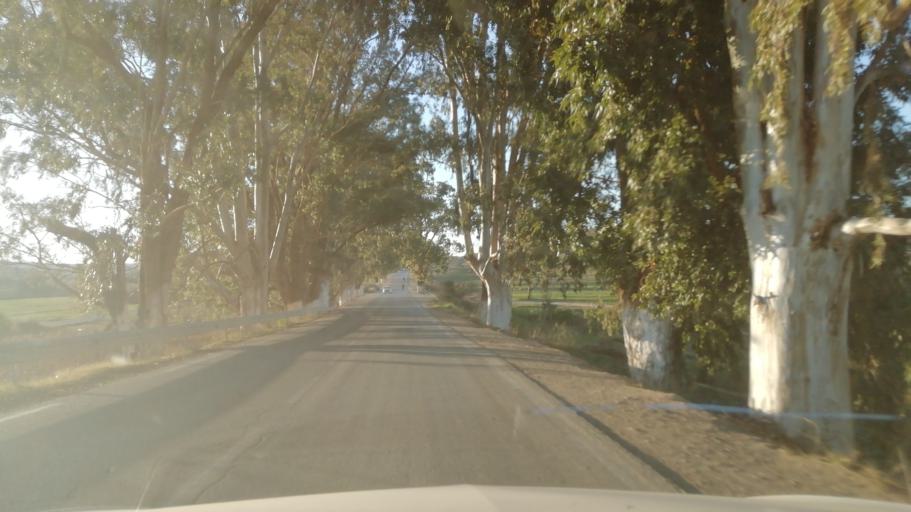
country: DZ
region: Tlemcen
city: Nedroma
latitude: 34.8263
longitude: -1.6548
